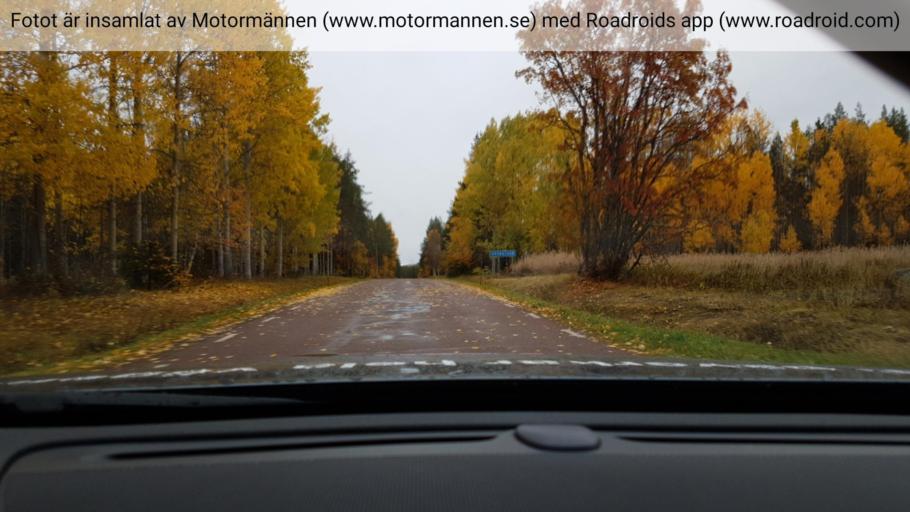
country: SE
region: Norrbotten
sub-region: Pajala Kommun
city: Pajala
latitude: 66.9377
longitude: 22.9809
